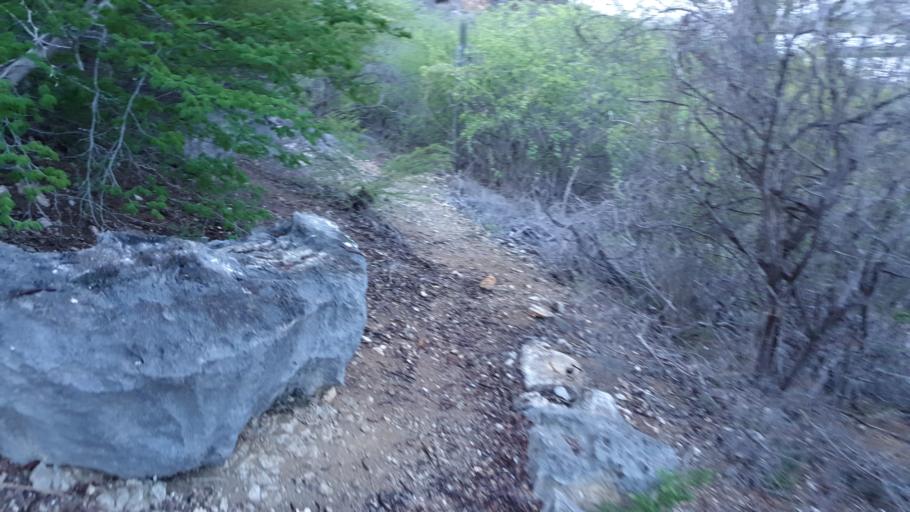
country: CW
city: Newport
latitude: 12.1295
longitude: -68.8145
